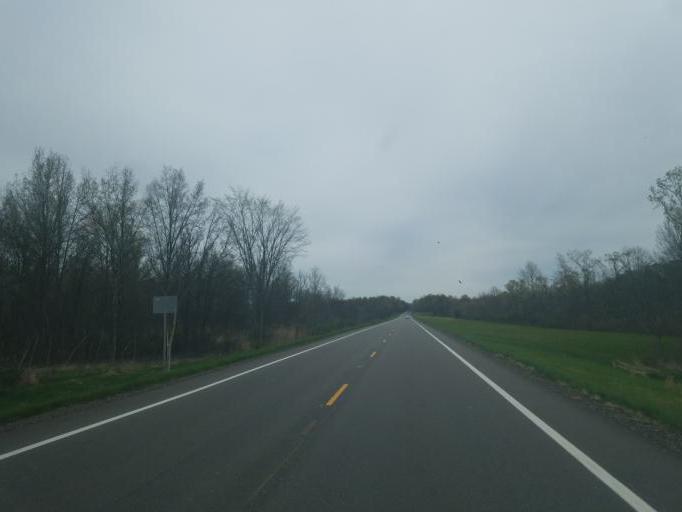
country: US
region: Ohio
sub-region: Wayne County
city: Doylestown
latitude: 40.9706
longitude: -81.7083
